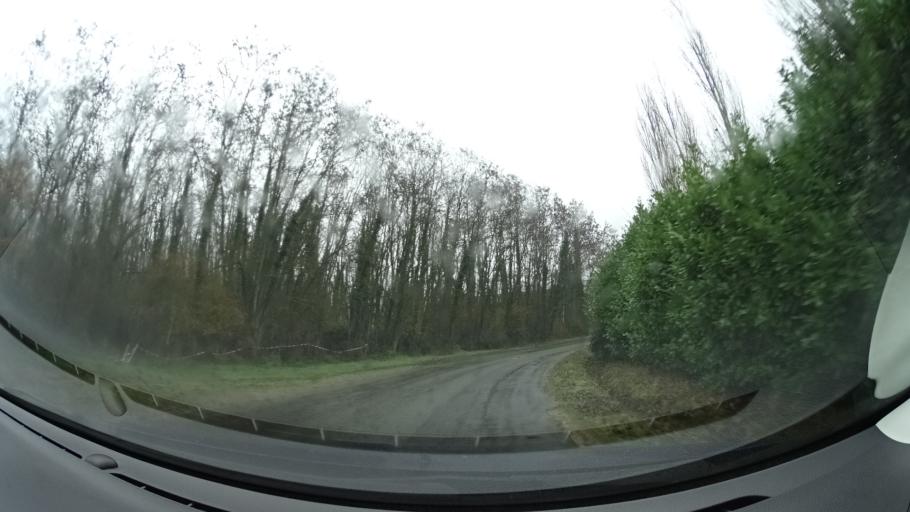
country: FR
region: Aquitaine
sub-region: Departement de la Dordogne
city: Cenac-et-Saint-Julien
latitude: 44.8288
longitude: 1.1635
